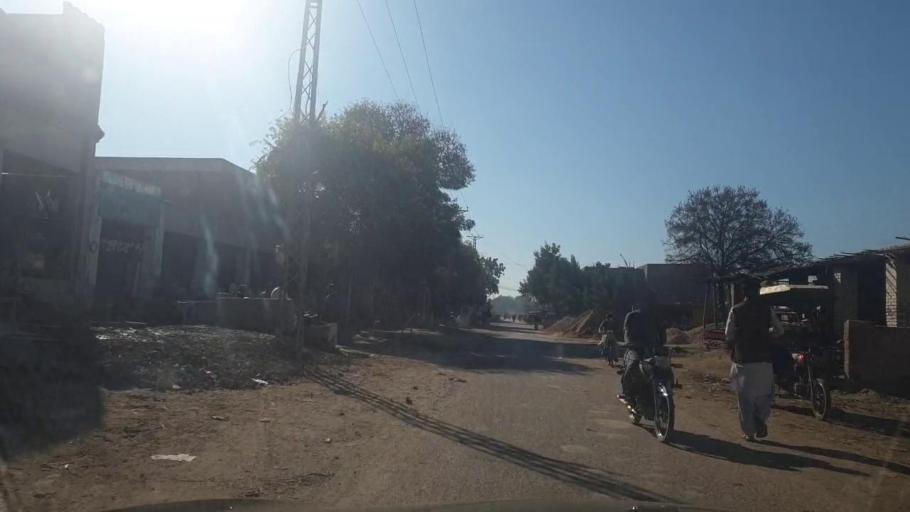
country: PK
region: Sindh
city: Ghotki
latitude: 27.9920
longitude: 69.3164
